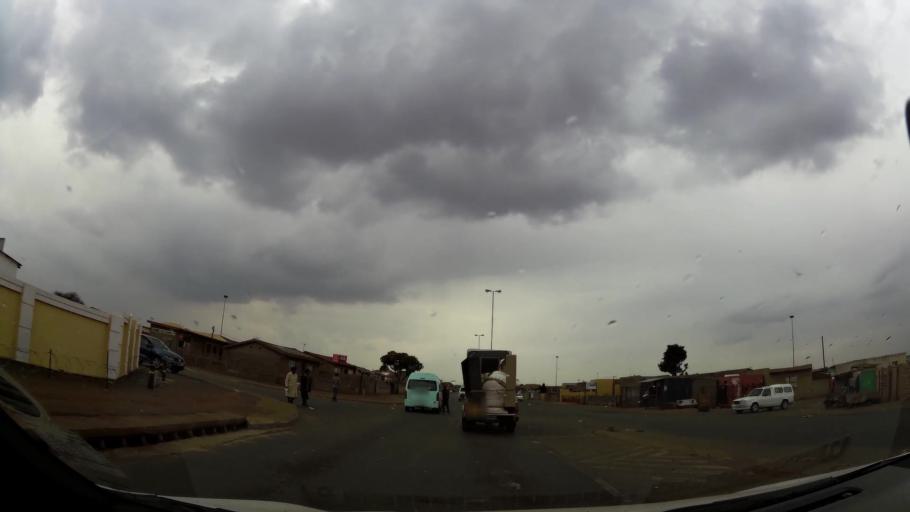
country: ZA
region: Gauteng
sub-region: Ekurhuleni Metropolitan Municipality
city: Germiston
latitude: -26.3521
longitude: 28.1498
